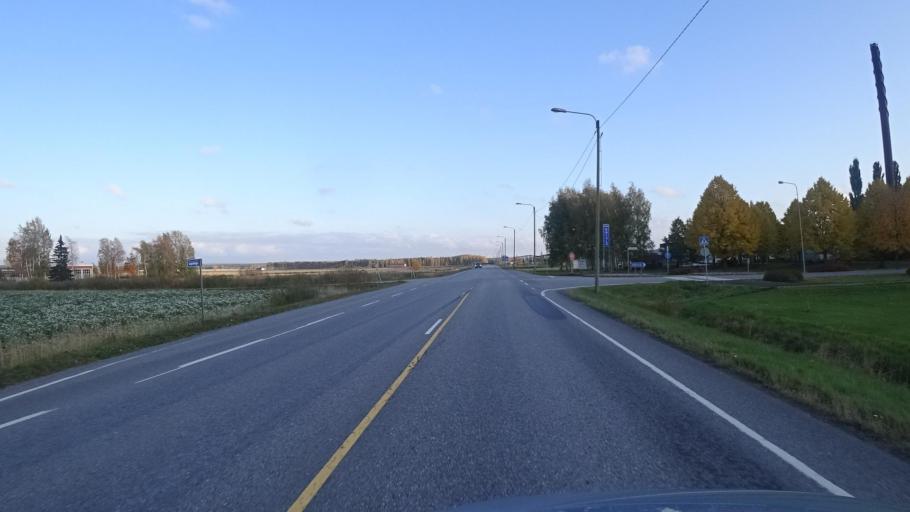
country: FI
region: Satakunta
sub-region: Rauma
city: Saekylae
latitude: 61.0491
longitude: 22.3501
